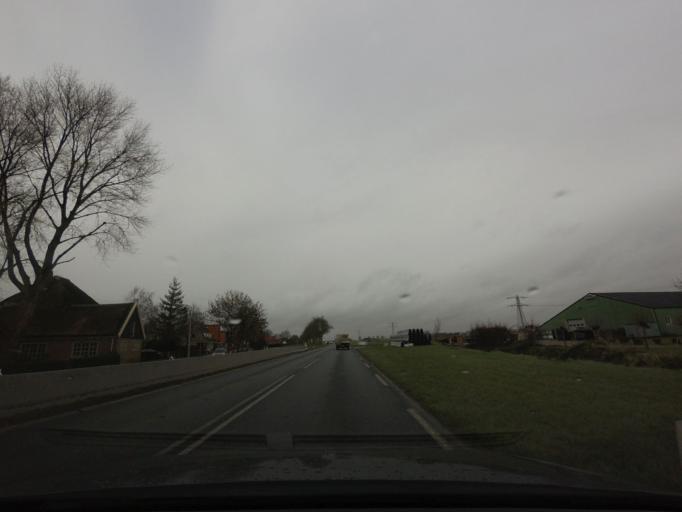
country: NL
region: North Holland
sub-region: Gemeente Schagen
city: Harenkarspel
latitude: 52.7378
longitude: 4.8418
